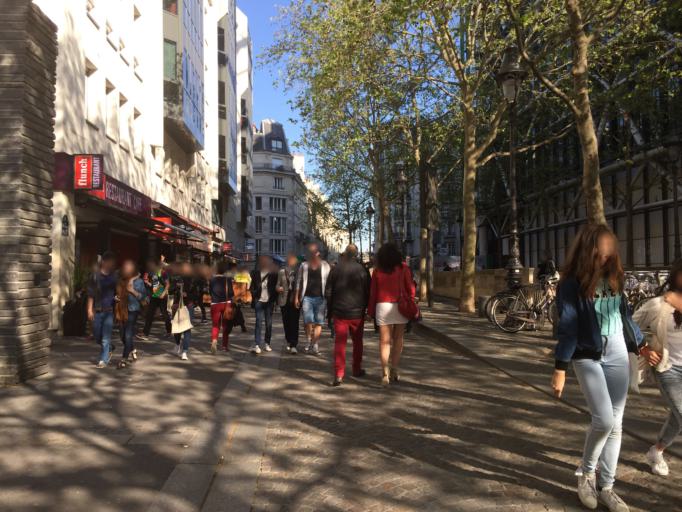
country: FR
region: Ile-de-France
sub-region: Paris
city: Paris
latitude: 48.8615
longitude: 2.3525
